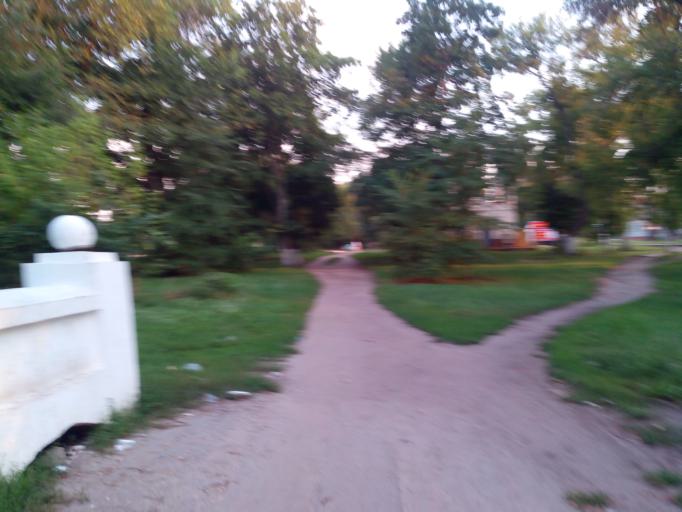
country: RU
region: Voronezj
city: Borisoglebsk
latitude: 51.3603
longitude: 42.0760
